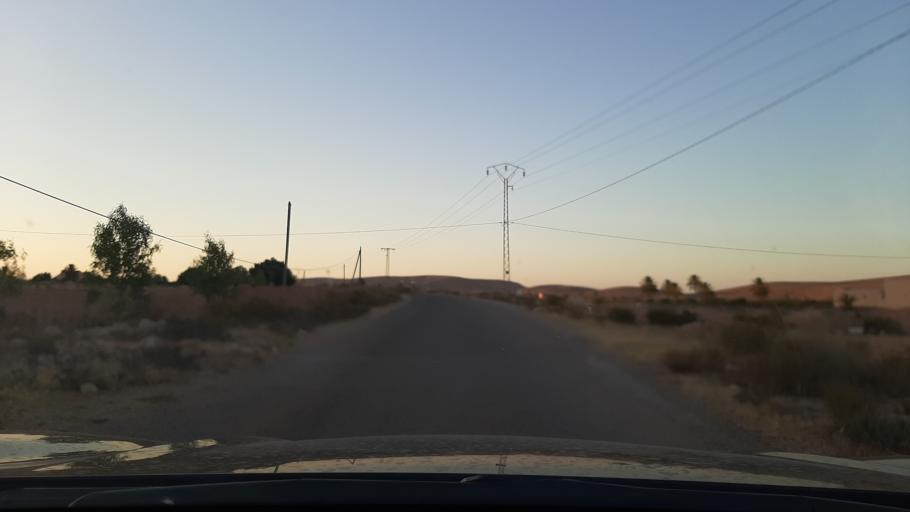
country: TN
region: Qabis
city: Matmata
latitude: 33.5549
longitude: 10.1858
